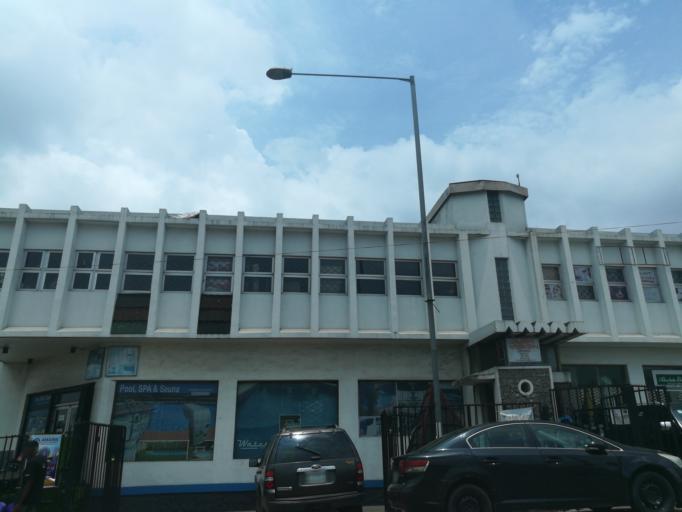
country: NG
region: Lagos
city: Ojota
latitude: 6.5972
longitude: 3.3666
